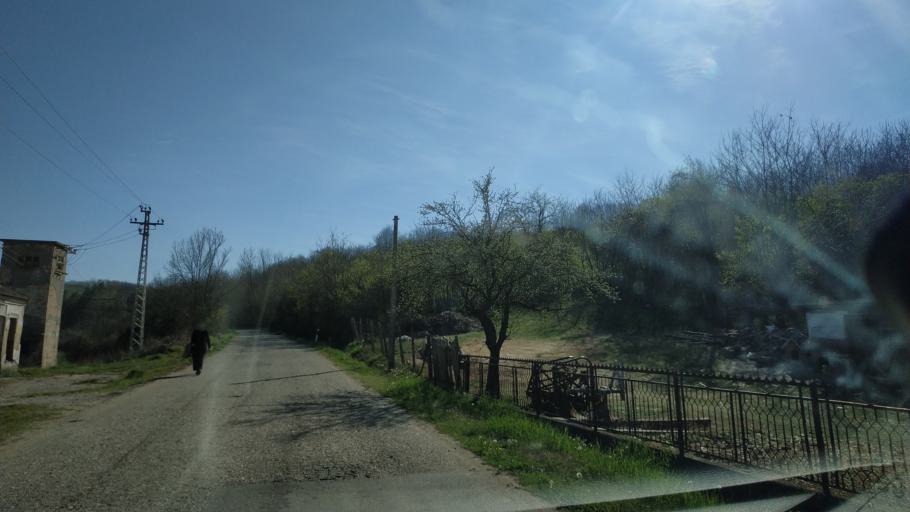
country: RS
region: Central Serbia
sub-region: Nisavski Okrug
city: Aleksinac
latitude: 43.4801
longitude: 21.6530
